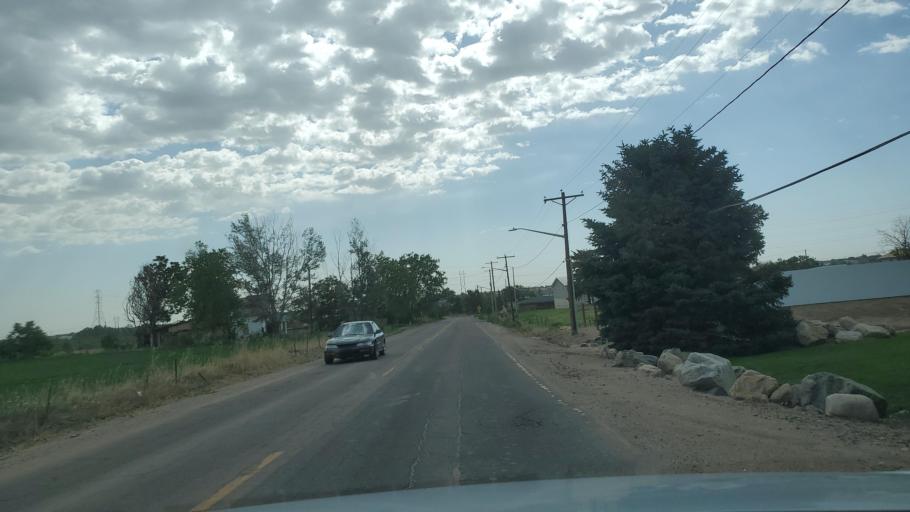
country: US
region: Colorado
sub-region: Adams County
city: Welby
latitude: 39.8381
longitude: -104.9539
